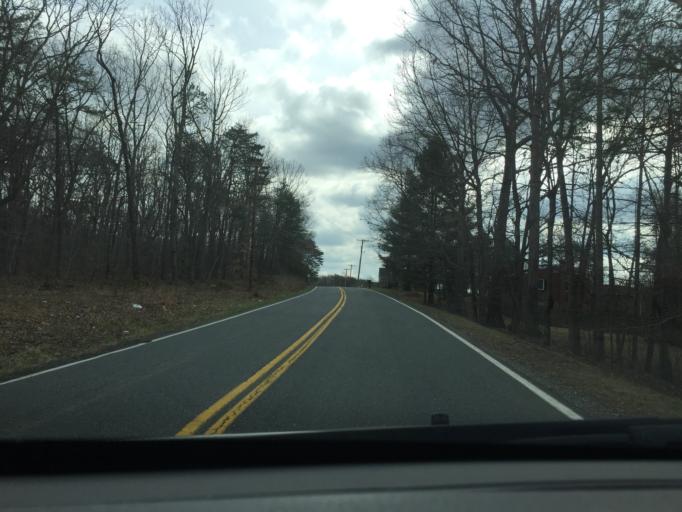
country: US
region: Virginia
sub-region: City of Lynchburg
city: West Lynchburg
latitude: 37.3303
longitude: -79.1661
